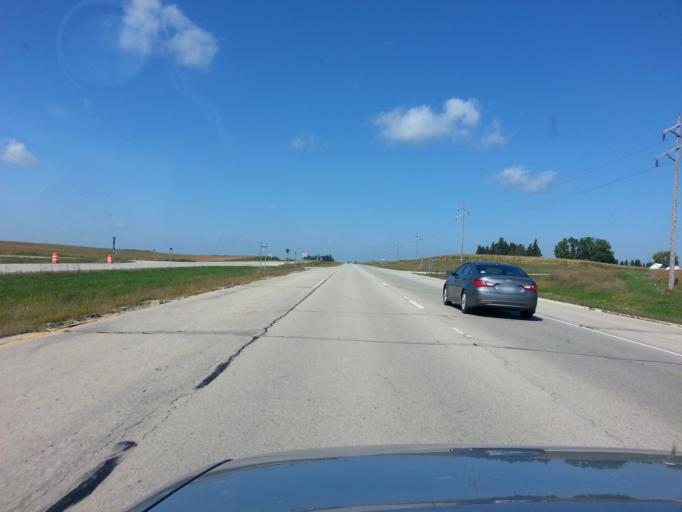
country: US
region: Minnesota
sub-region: Goodhue County
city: Wanamingo
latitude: 44.4039
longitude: -92.8502
